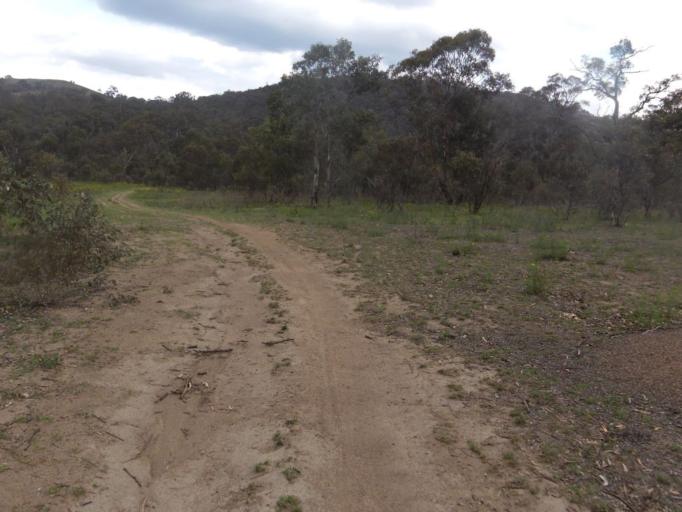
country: AU
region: Australian Capital Territory
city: Forrest
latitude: -35.3538
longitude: 149.1175
